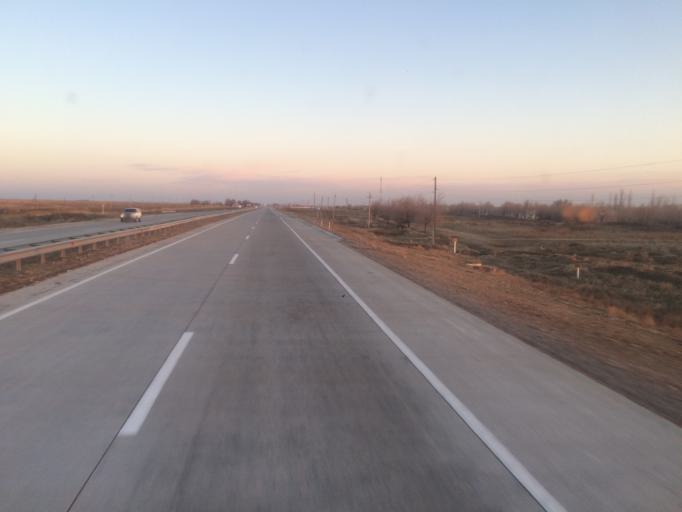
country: KZ
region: Ongtustik Qazaqstan
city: Bayaldyr
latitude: 43.0664
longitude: 68.6738
